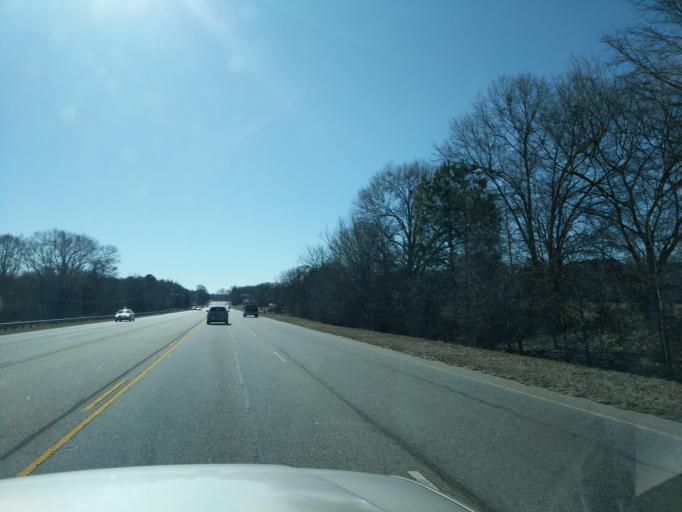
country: US
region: South Carolina
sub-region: Anderson County
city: Northlake
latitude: 34.6159
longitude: -82.6083
